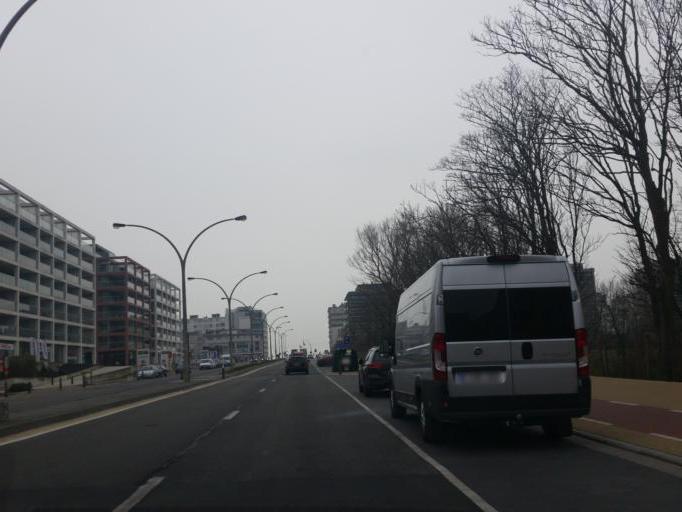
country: BE
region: Flanders
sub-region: Provincie West-Vlaanderen
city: Ostend
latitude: 51.2171
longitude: 2.8905
